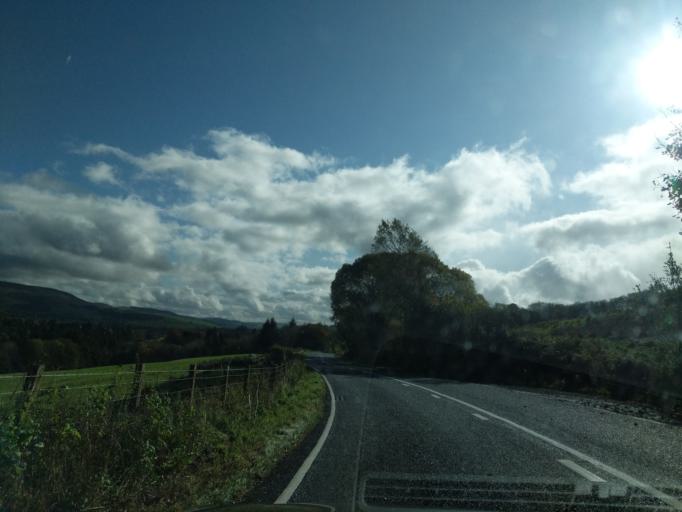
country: GB
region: Scotland
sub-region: Dumfries and Galloway
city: Moffat
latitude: 55.3445
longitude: -3.4603
